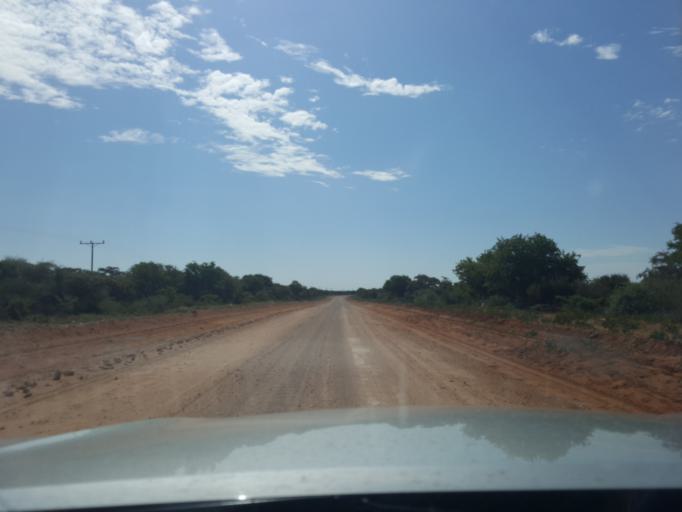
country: BW
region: Kweneng
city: Khudumelapye
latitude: -23.8047
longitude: 24.8115
